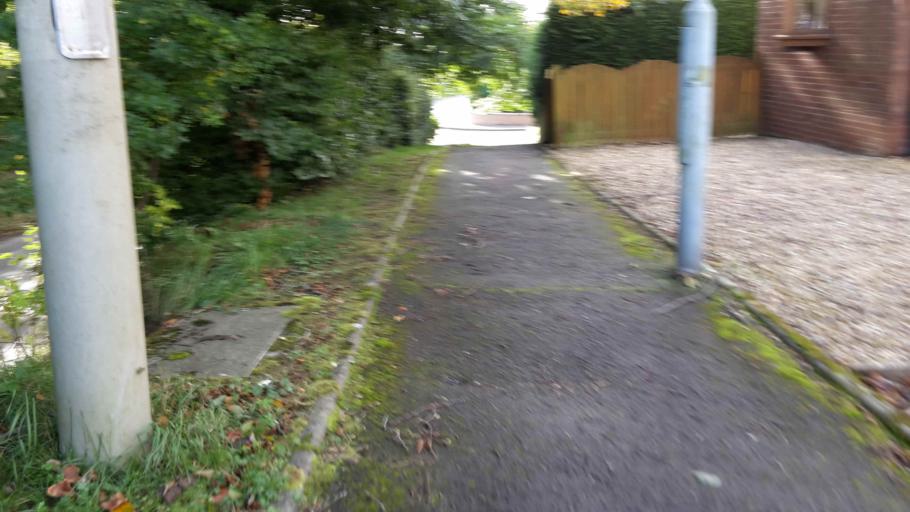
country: GB
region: Scotland
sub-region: South Lanarkshire
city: Carluke
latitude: 55.7245
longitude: -3.8280
